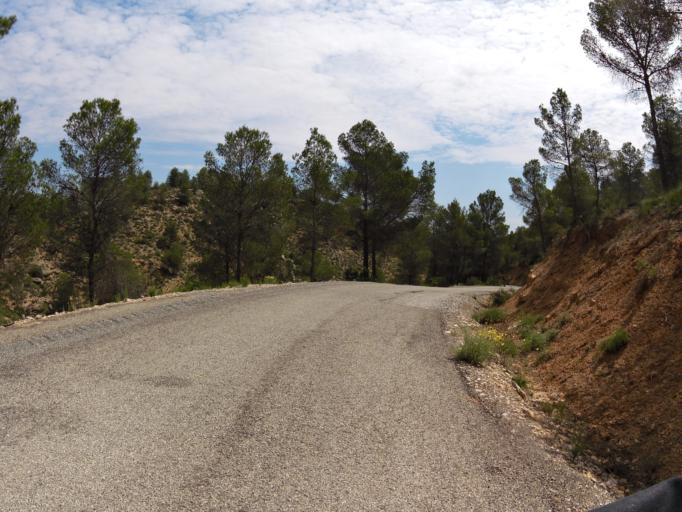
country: ES
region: Castille-La Mancha
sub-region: Provincia de Albacete
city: Casas Ibanez
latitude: 39.3683
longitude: -1.4561
